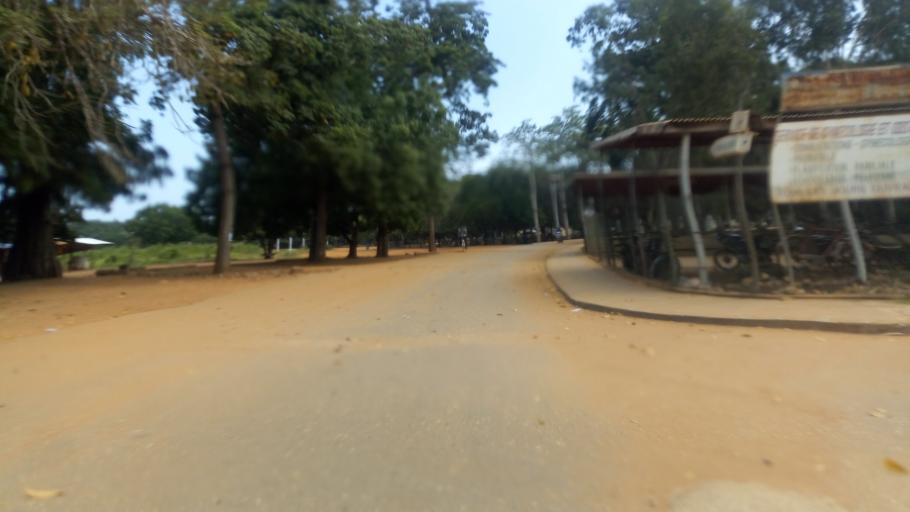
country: TG
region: Maritime
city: Lome
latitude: 6.1793
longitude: 1.2132
